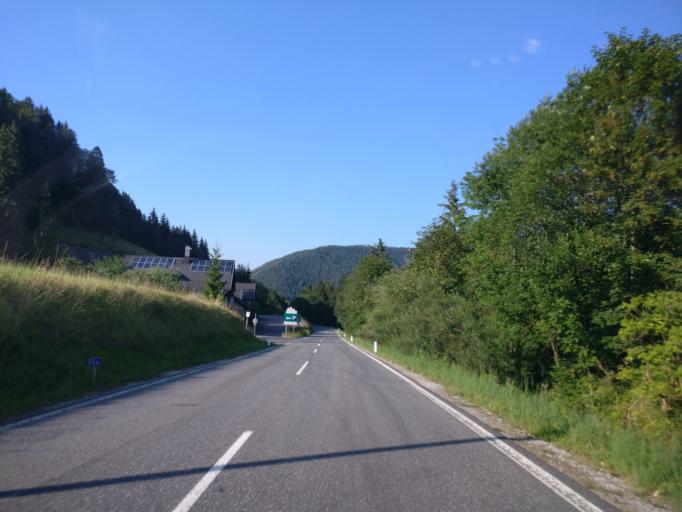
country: AT
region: Lower Austria
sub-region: Politischer Bezirk Scheibbs
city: Gostling an der Ybbs
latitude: 47.7548
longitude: 14.9019
